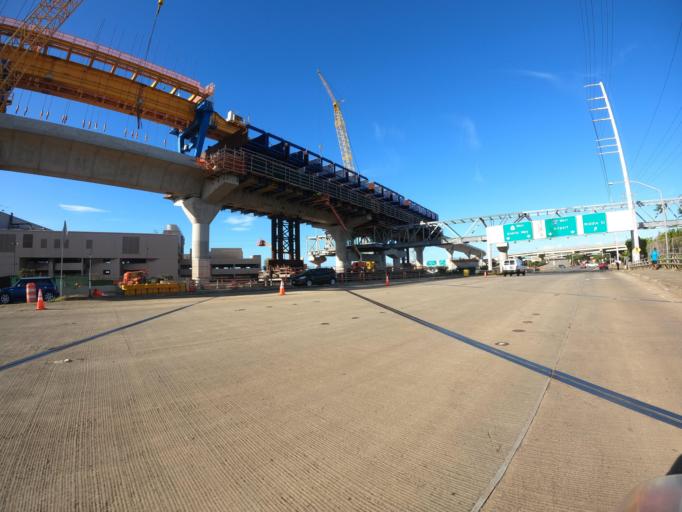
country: US
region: Hawaii
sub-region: Honolulu County
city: Honolulu
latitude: 21.3330
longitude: -157.8882
